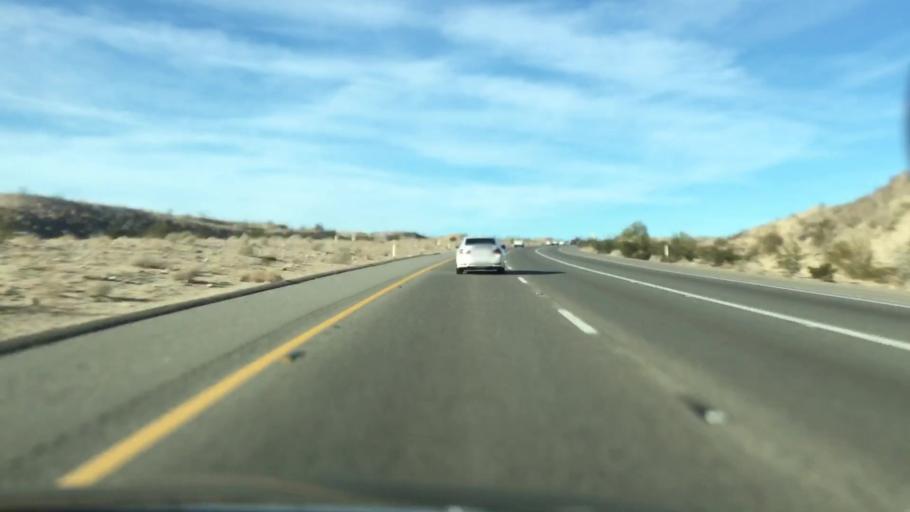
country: US
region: California
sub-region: San Bernardino County
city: Fort Irwin
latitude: 35.0871
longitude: -116.3280
